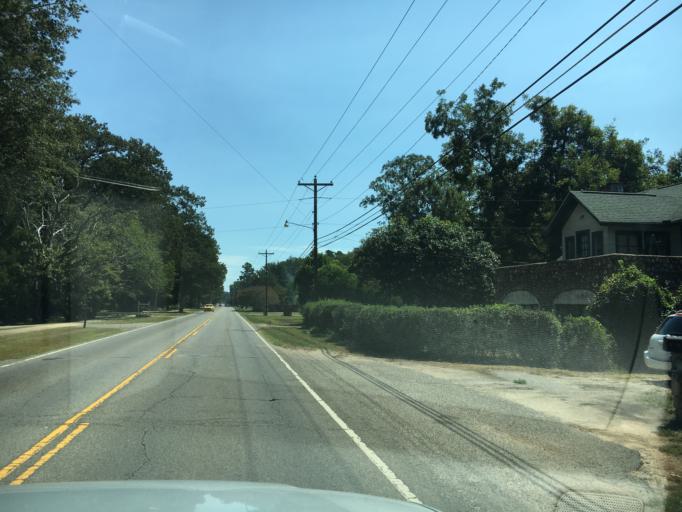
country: US
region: South Carolina
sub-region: Edgefield County
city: Johnston
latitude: 33.8485
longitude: -81.6740
